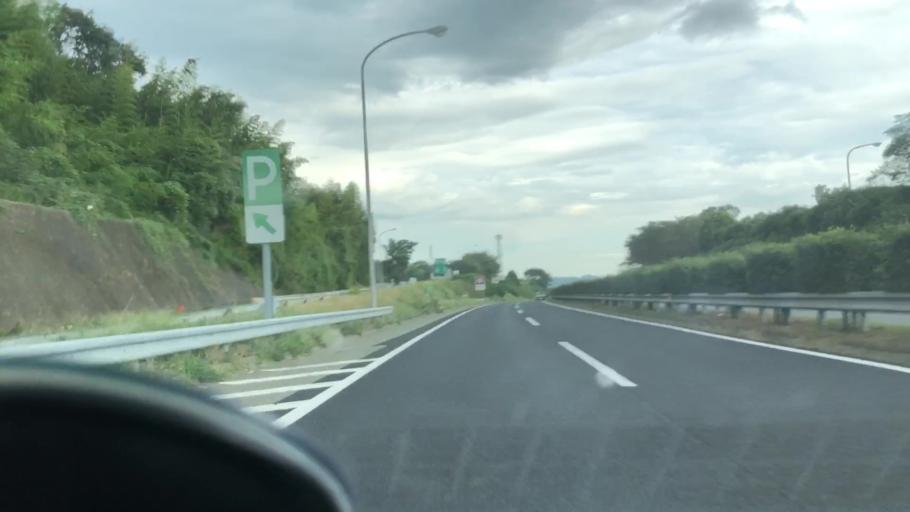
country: JP
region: Hyogo
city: Himeji
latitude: 34.9478
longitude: 134.7986
